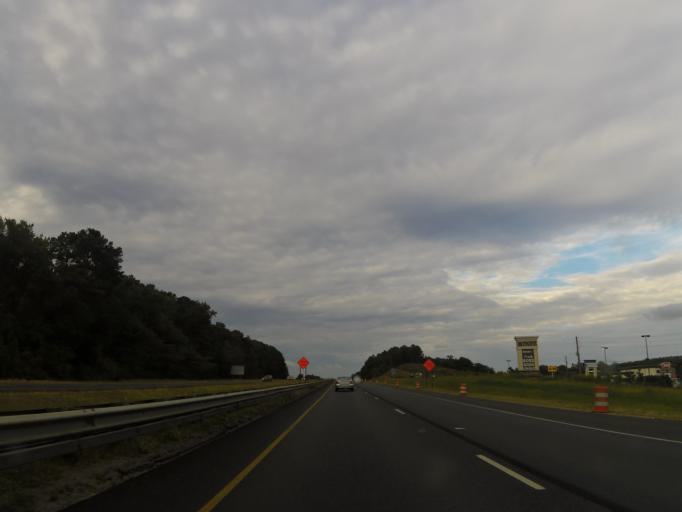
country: US
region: Alabama
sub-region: Shelby County
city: Alabaster
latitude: 33.2373
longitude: -86.8038
